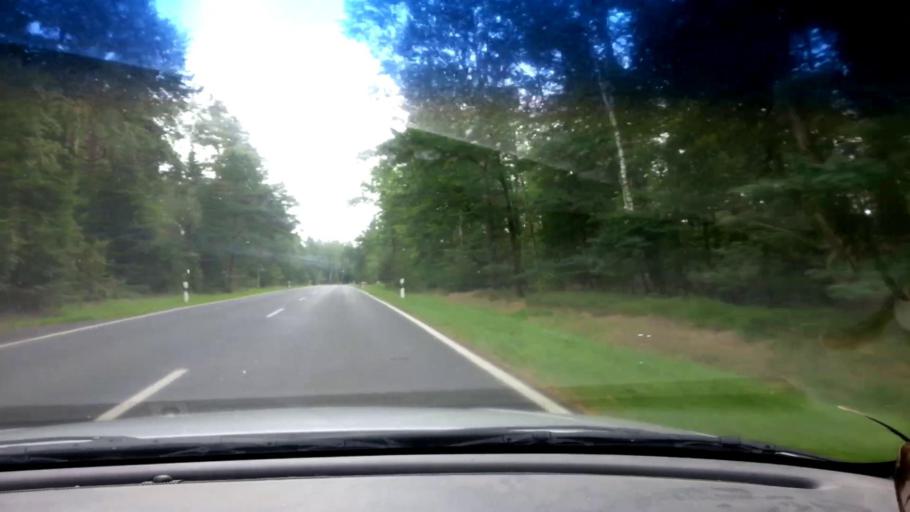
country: DE
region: Bavaria
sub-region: Upper Franconia
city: Schirnding
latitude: 50.0742
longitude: 12.2364
